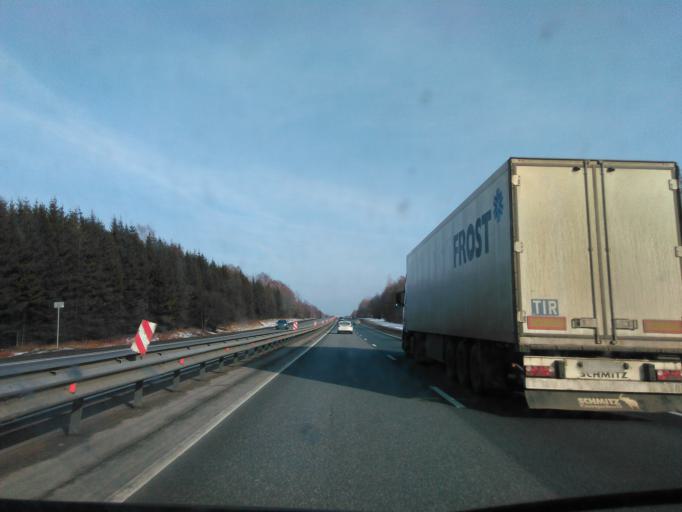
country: RU
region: Smolensk
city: Kholm-Zhirkovskiy
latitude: 55.1841
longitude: 33.7008
